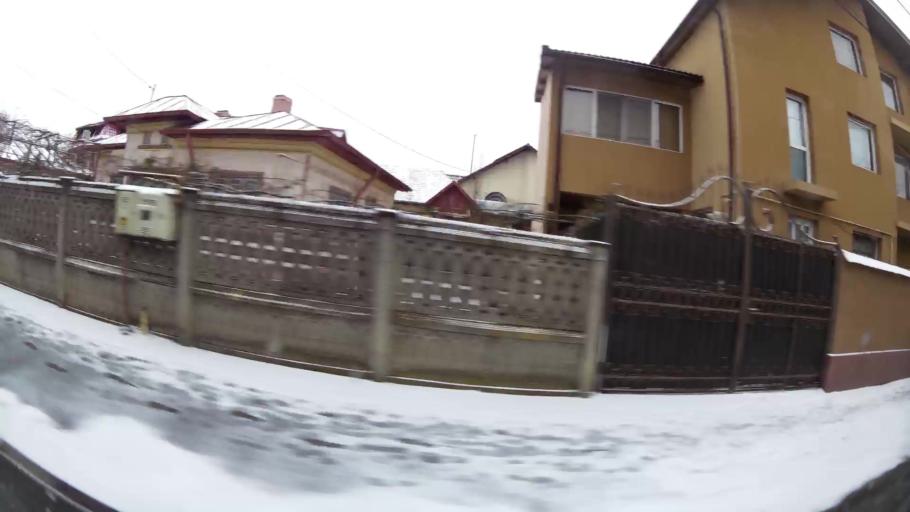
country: RO
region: Dambovita
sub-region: Municipiul Targoviste
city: Targoviste
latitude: 44.9309
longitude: 25.4557
